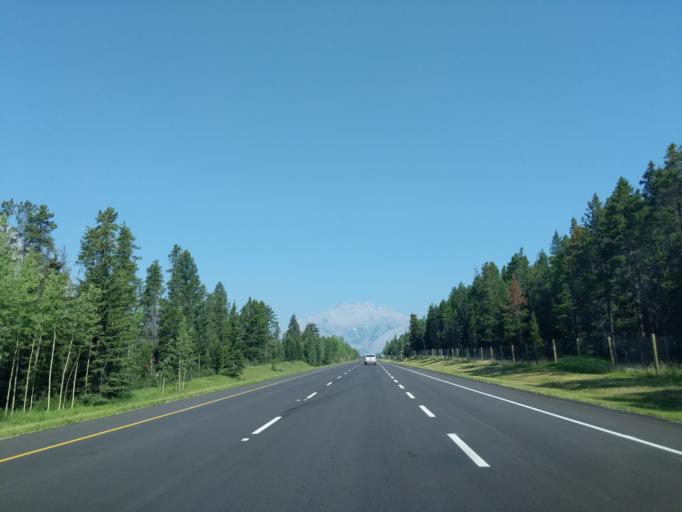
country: CA
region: Alberta
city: Canmore
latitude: 51.1428
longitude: -115.4174
